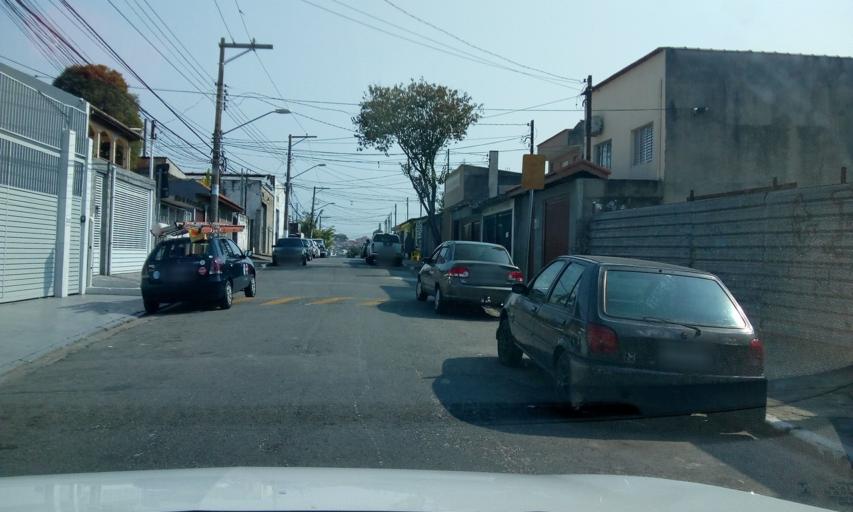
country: BR
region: Sao Paulo
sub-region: Diadema
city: Diadema
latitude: -23.7156
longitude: -46.6936
